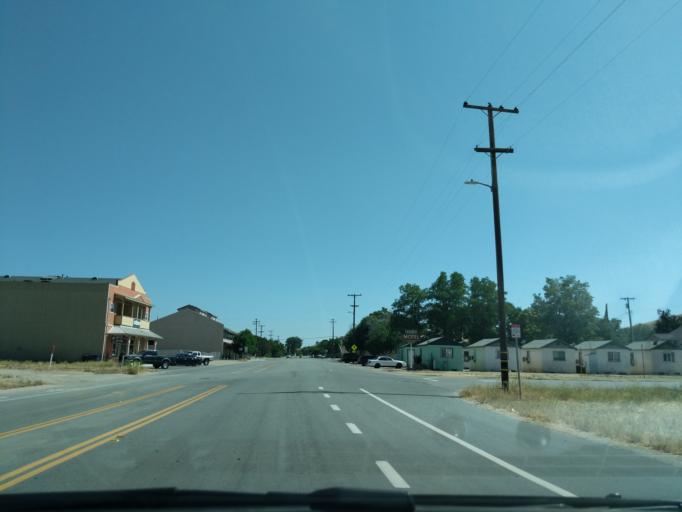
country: US
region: California
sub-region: San Luis Obispo County
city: San Miguel
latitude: 35.7544
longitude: -120.6959
